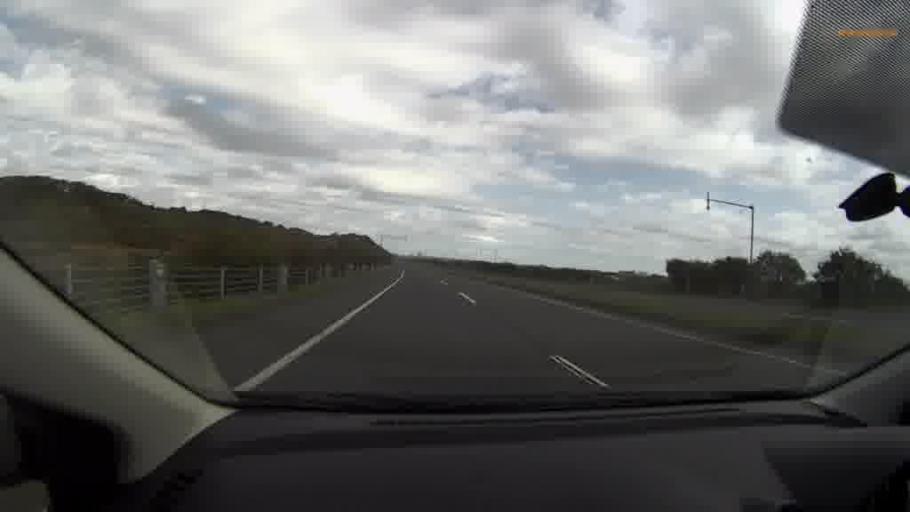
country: JP
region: Hokkaido
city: Kushiro
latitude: 43.0100
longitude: 144.2565
